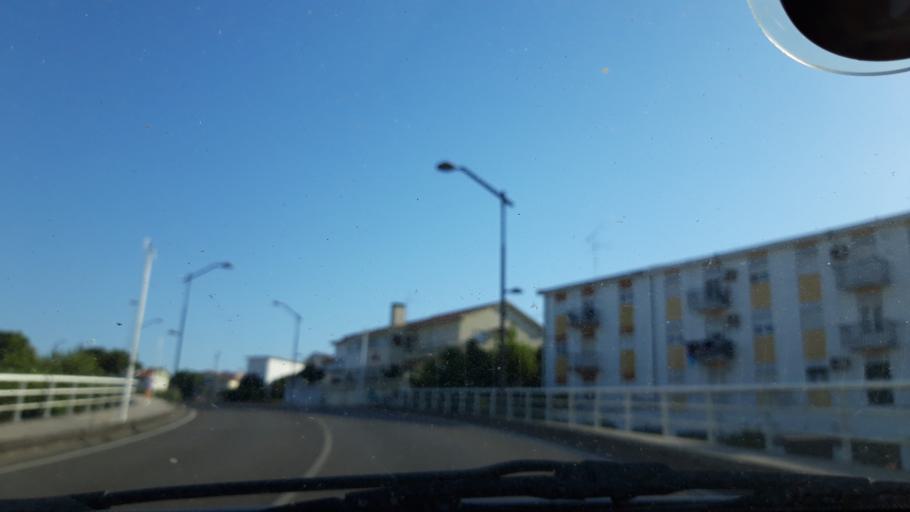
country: PT
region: Santarem
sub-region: Torres Novas
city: Torres Novas
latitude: 39.4792
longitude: -8.5460
